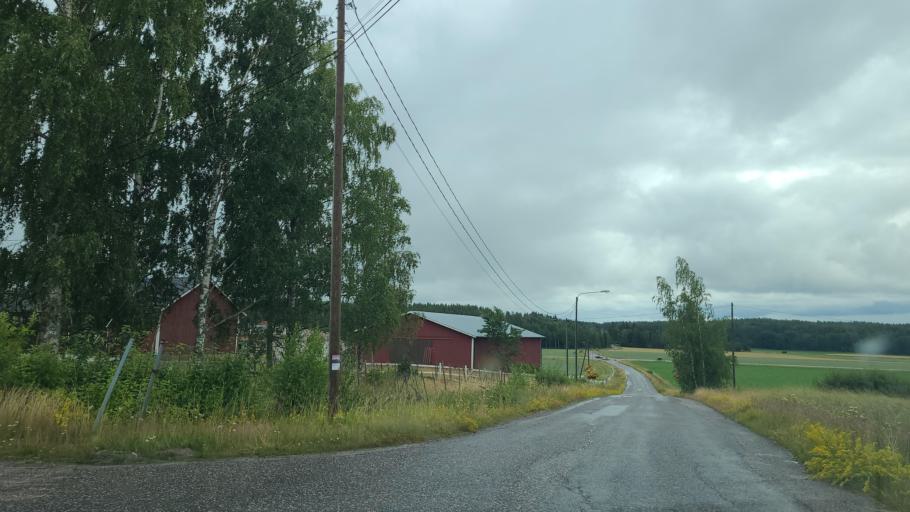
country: FI
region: Varsinais-Suomi
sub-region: Aboland-Turunmaa
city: Kimito
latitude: 60.1709
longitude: 22.7512
